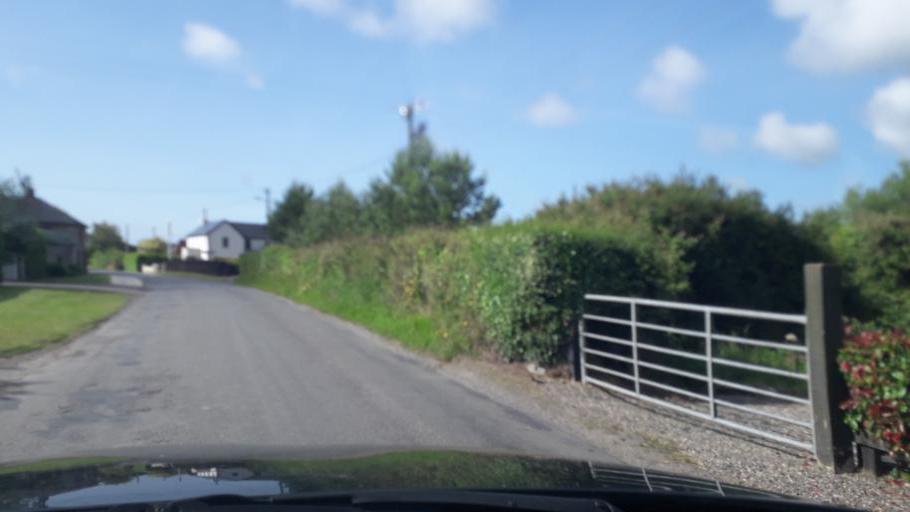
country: IE
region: Leinster
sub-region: Loch Garman
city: Loch Garman
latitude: 52.2447
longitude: -6.5505
